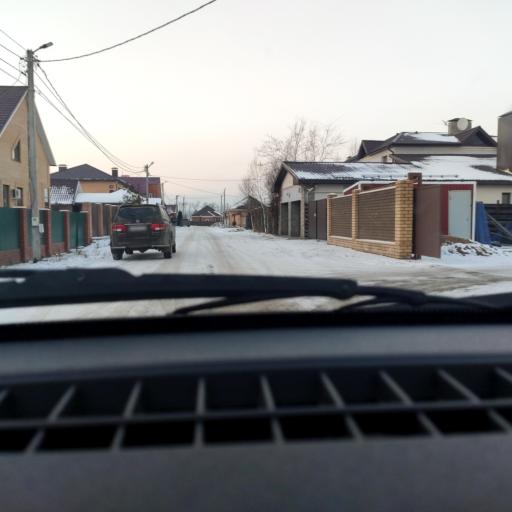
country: RU
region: Bashkortostan
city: Mikhaylovka
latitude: 54.8091
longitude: 55.9416
